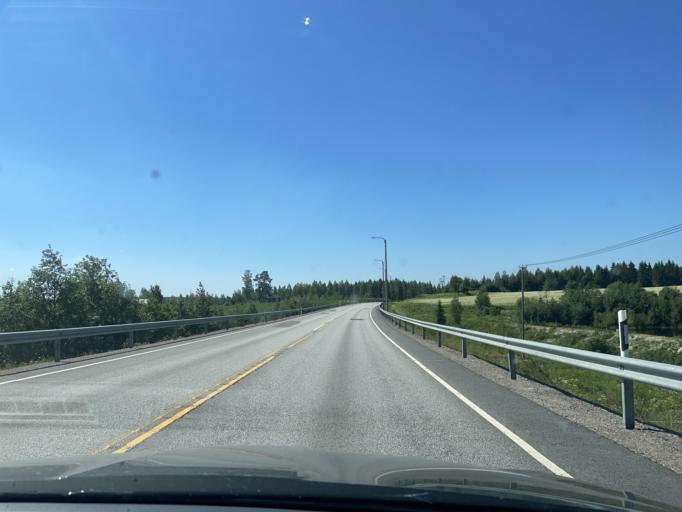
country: FI
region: Central Finland
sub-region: Saarijaervi-Viitasaari
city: Viitasaari
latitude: 63.1437
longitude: 25.8510
